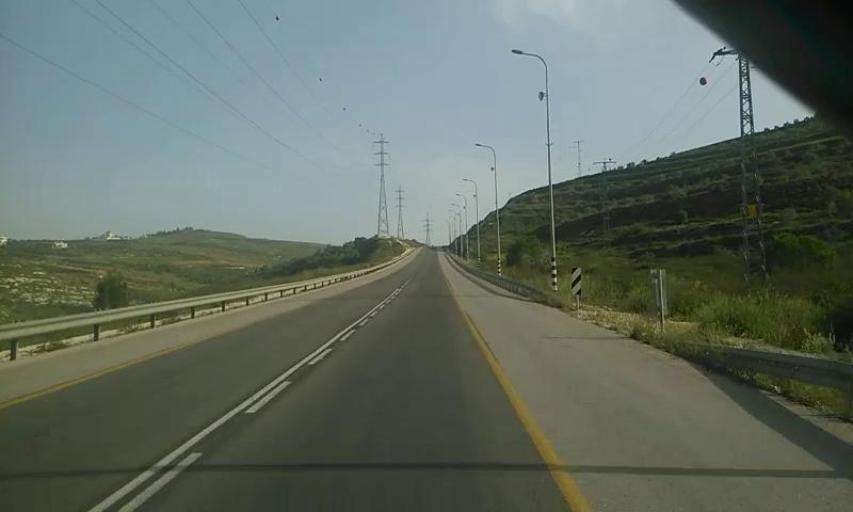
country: PS
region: West Bank
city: Sarrah
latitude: 32.2103
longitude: 35.1814
